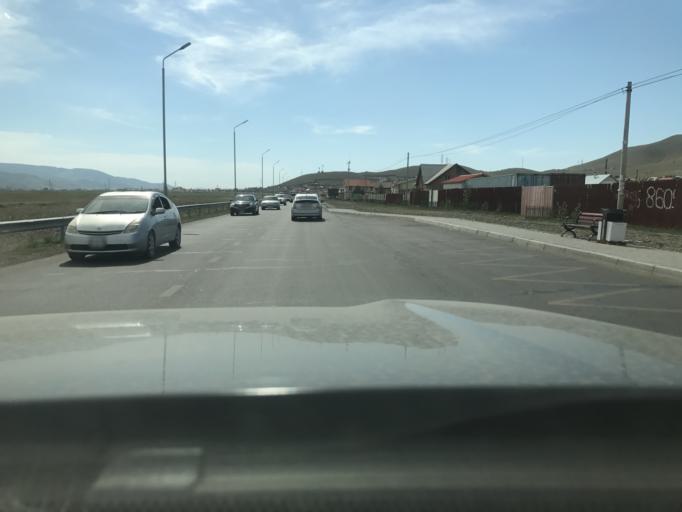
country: MN
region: Ulaanbaatar
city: Ulaanbaatar
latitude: 47.9156
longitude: 107.0681
